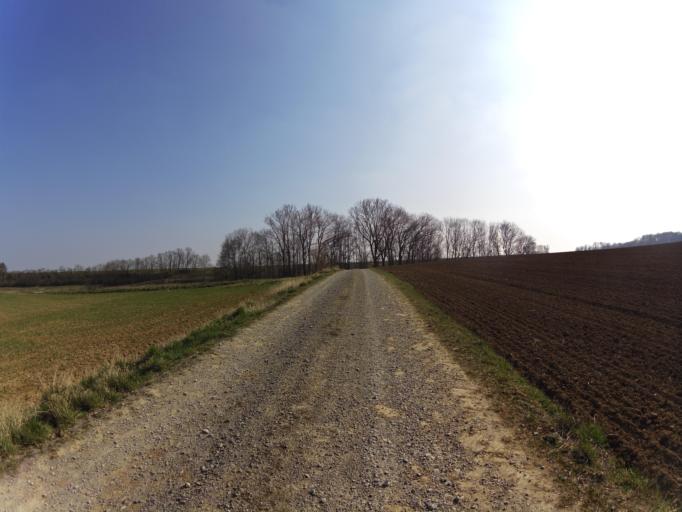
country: DE
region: Bavaria
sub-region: Regierungsbezirk Unterfranken
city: Gaukonigshofen
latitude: 49.6661
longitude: 9.9880
